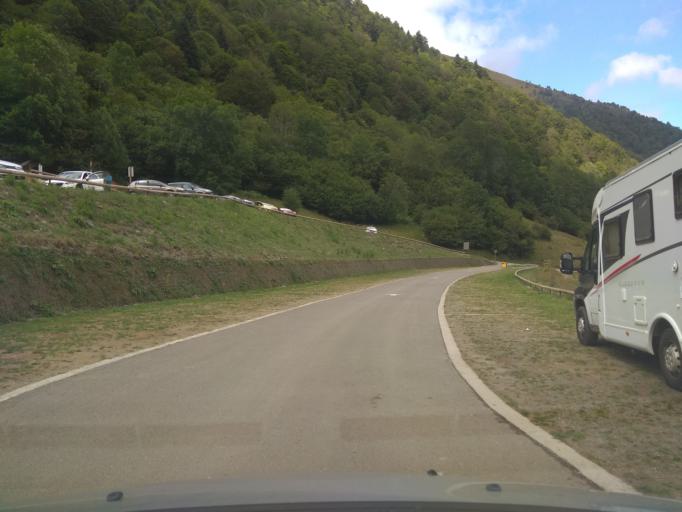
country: ES
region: Catalonia
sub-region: Provincia de Lleida
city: Vielha
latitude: 42.6971
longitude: 0.7086
